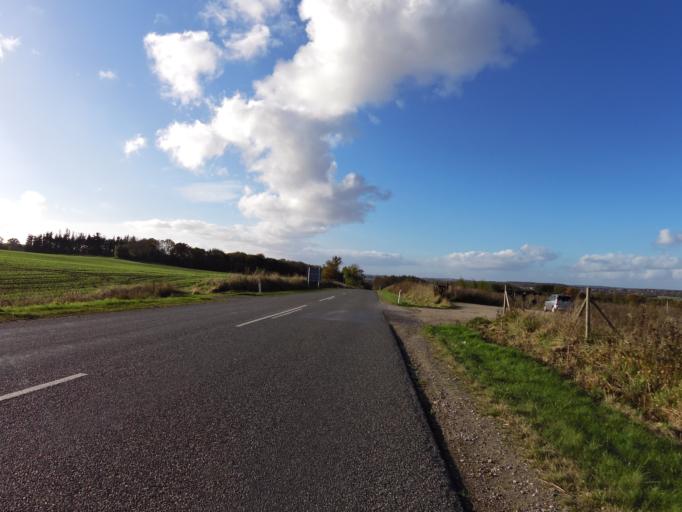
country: DK
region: Central Jutland
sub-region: Skanderborg Kommune
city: Horning
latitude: 56.1224
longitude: 10.0309
